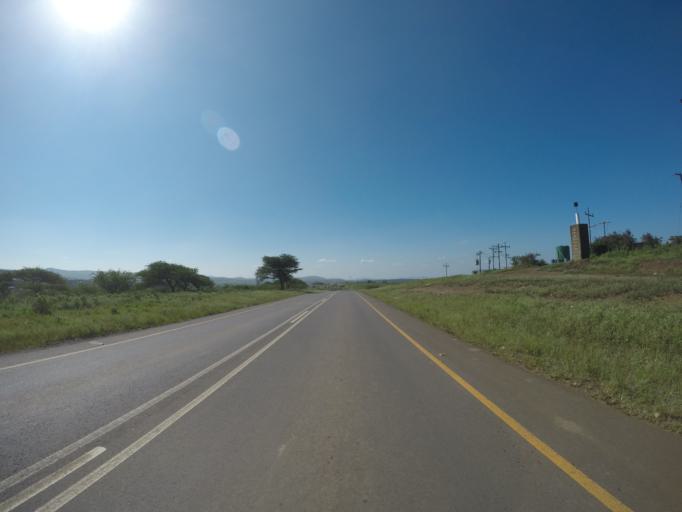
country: ZA
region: KwaZulu-Natal
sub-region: uThungulu District Municipality
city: Empangeni
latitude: -28.5659
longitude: 31.7091
